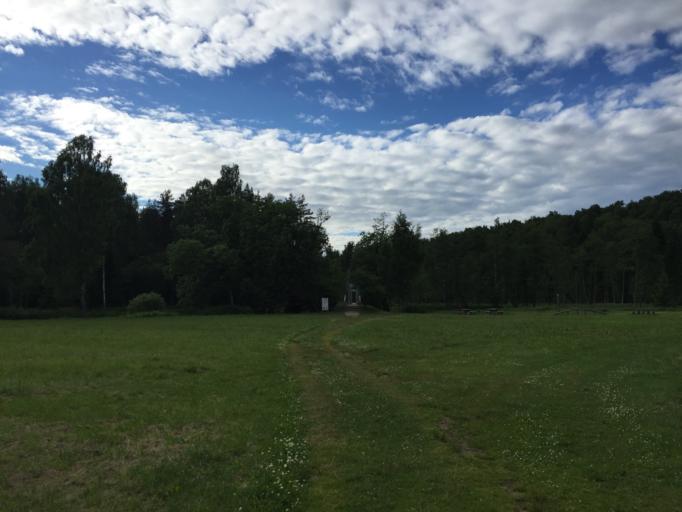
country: LV
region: Ligatne
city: Ligatne
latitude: 57.2465
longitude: 25.1443
